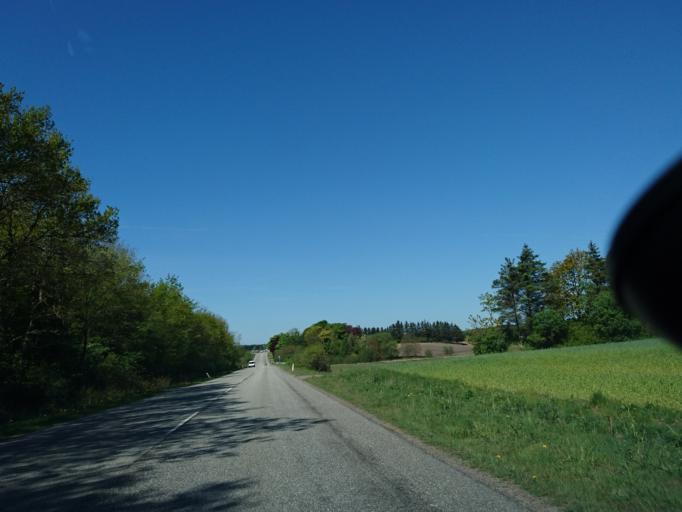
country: DK
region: North Denmark
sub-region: Hjorring Kommune
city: Sindal
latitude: 57.4662
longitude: 10.2675
